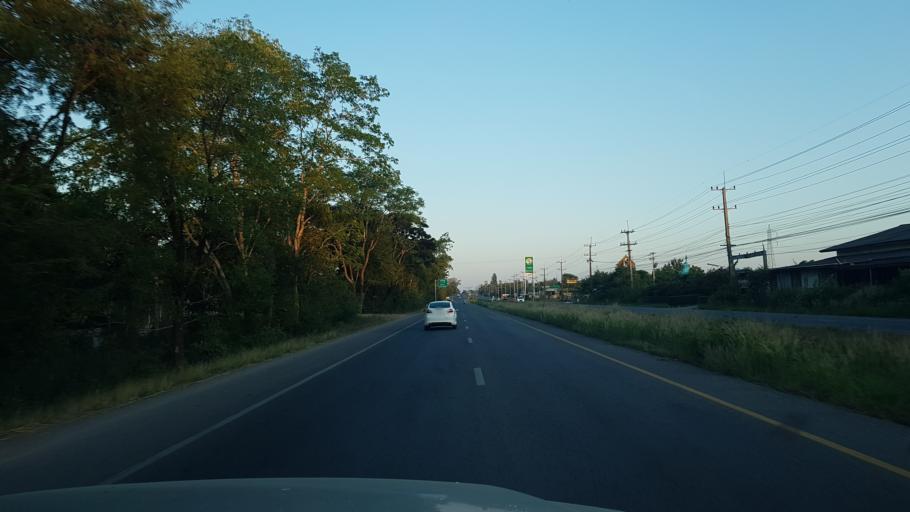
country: TH
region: Khon Kaen
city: Chum Phae
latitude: 16.5798
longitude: 102.0208
